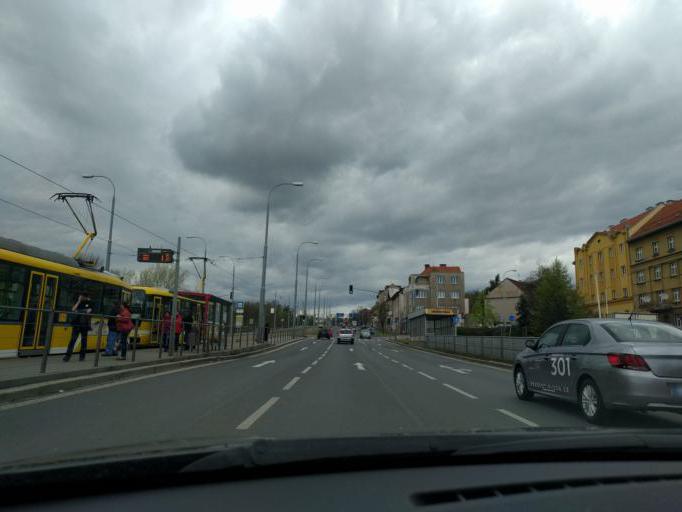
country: CZ
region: Plzensky
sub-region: Okres Plzen-Mesto
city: Pilsen
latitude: 49.7576
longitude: 13.3727
